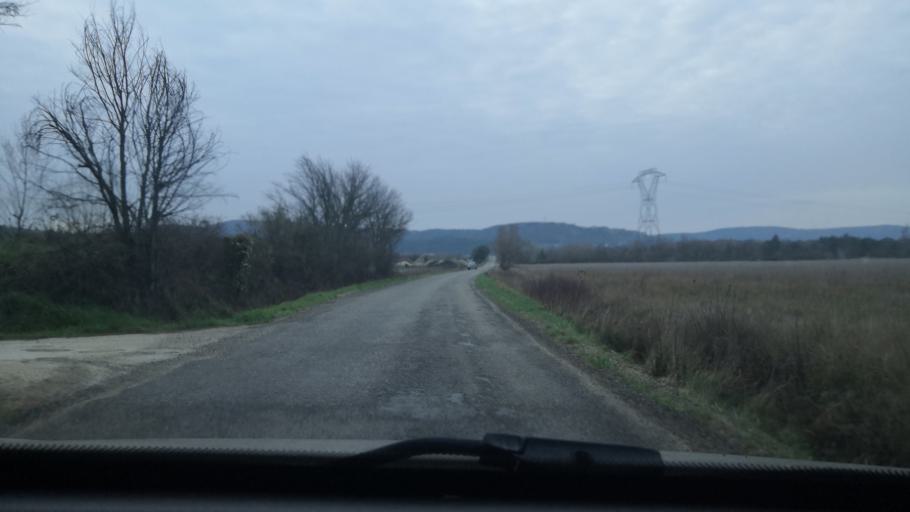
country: FR
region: Rhone-Alpes
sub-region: Departement de la Drome
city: Allan
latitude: 44.5235
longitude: 4.7823
